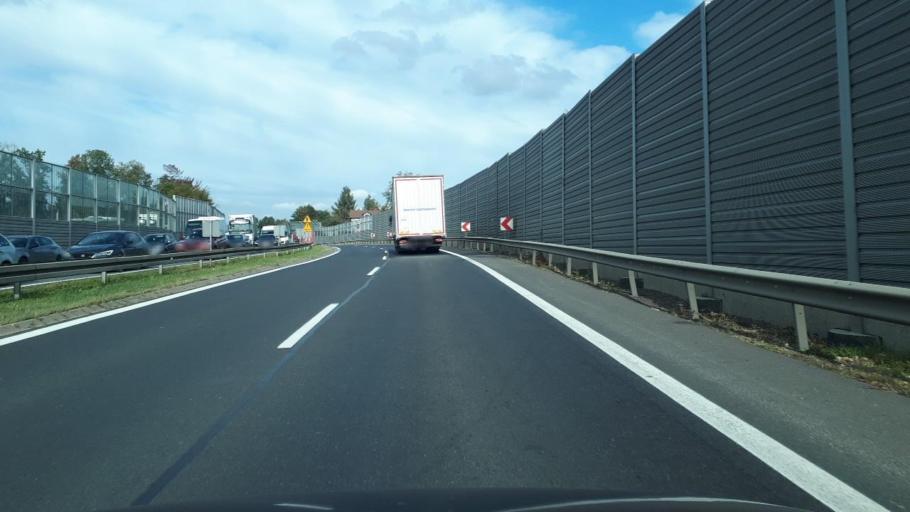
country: PL
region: Silesian Voivodeship
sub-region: Powiat bielski
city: Czechowice-Dziedzice
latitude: 49.9060
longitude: 18.9915
